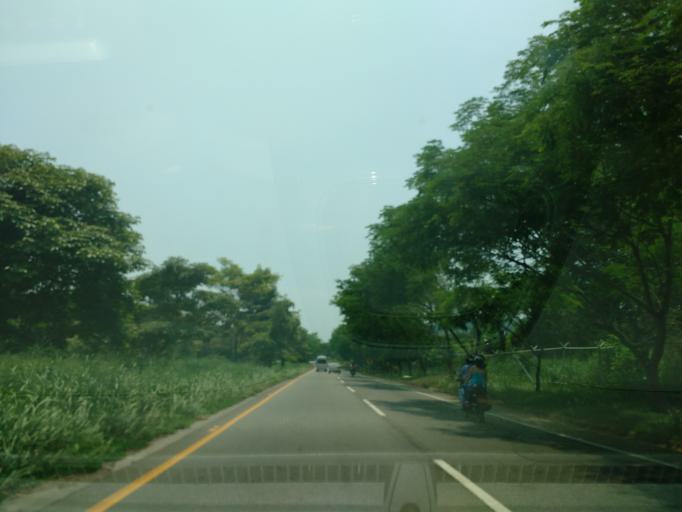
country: CO
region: Tolima
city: Melgar
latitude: 4.2175
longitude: -74.6623
